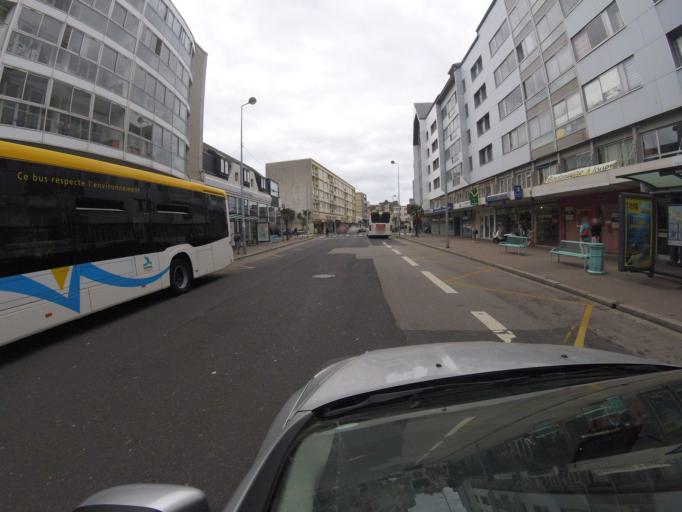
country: FR
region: Lower Normandy
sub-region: Departement de la Manche
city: Cherbourg-Octeville
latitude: 49.6369
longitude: -1.6256
